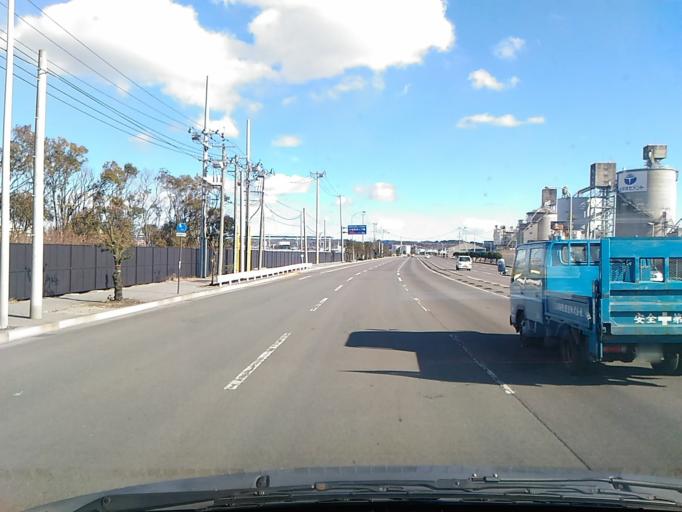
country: JP
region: Fukushima
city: Iwaki
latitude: 36.9416
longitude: 140.8886
